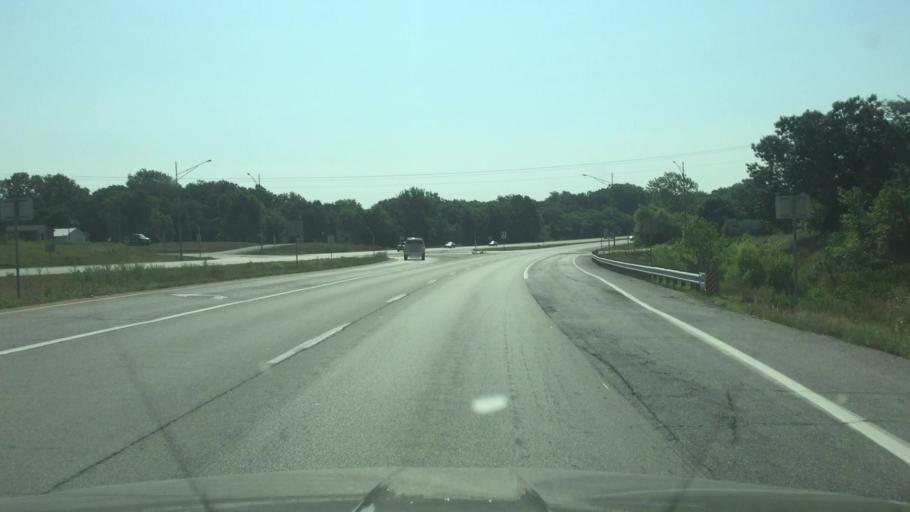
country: US
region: Missouri
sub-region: Jackson County
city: Lone Jack
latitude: 38.8683
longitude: -94.0613
